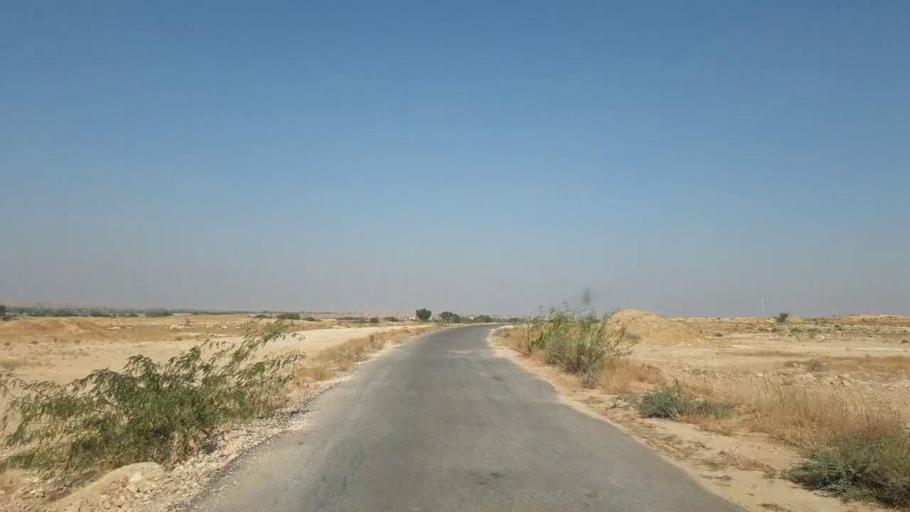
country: PK
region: Sindh
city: Thatta
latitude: 25.2046
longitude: 67.7975
